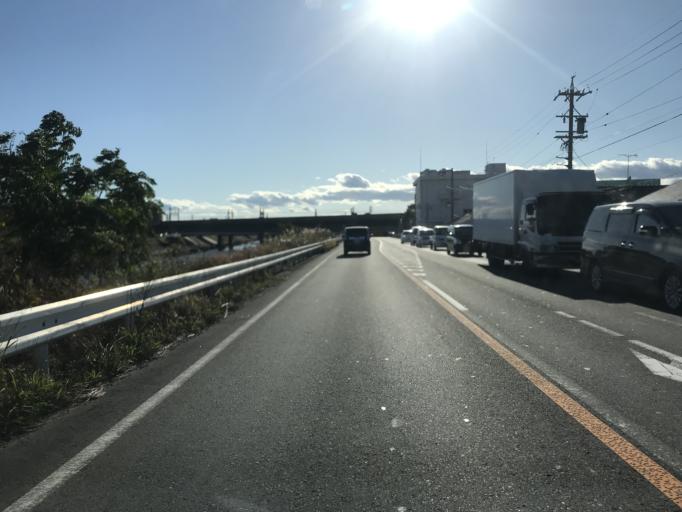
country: JP
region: Aichi
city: Nagoya-shi
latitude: 35.2054
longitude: 136.8574
